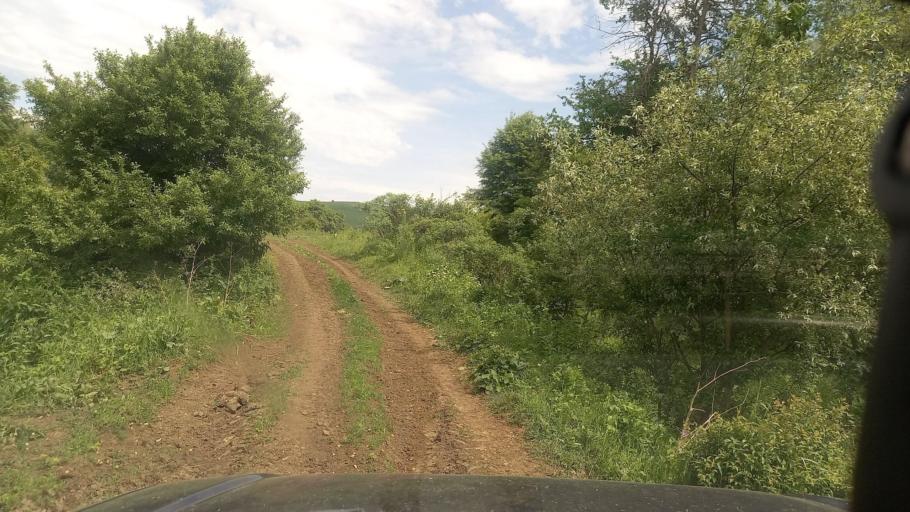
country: RU
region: Karachayevo-Cherkesiya
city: Pregradnaya
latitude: 44.0776
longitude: 41.2677
